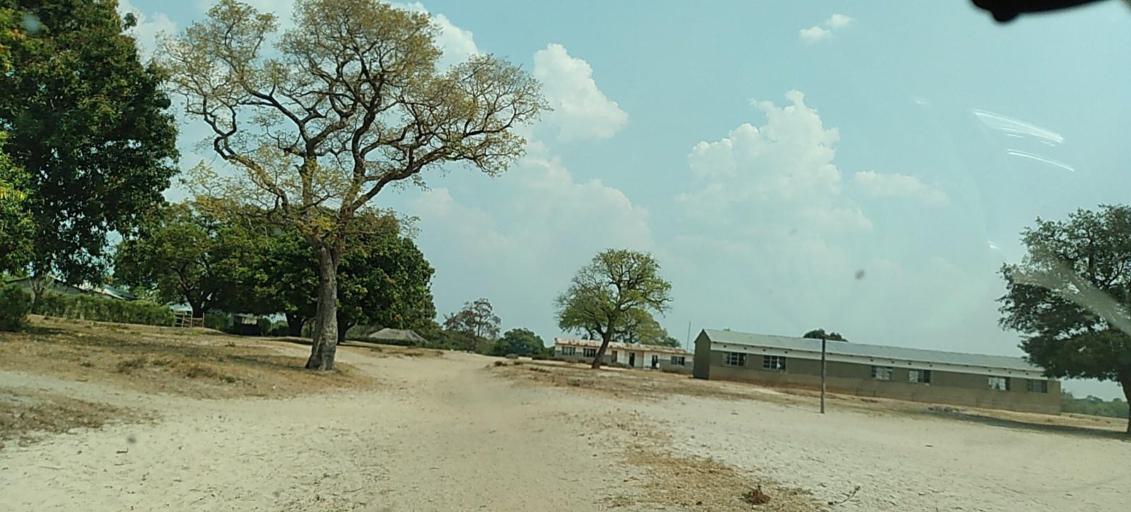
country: ZM
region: North-Western
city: Kabompo
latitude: -13.4491
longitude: 23.6674
